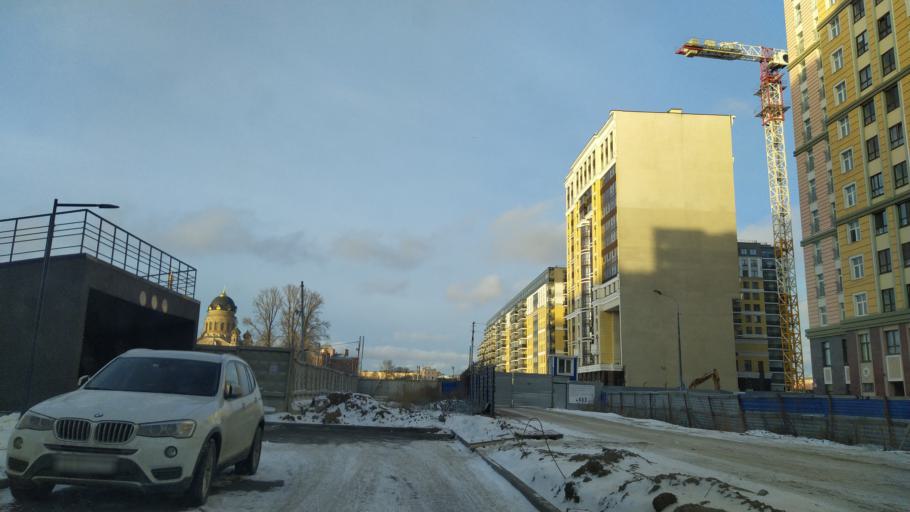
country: RU
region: St.-Petersburg
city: Admiralteisky
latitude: 59.9050
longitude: 30.3117
